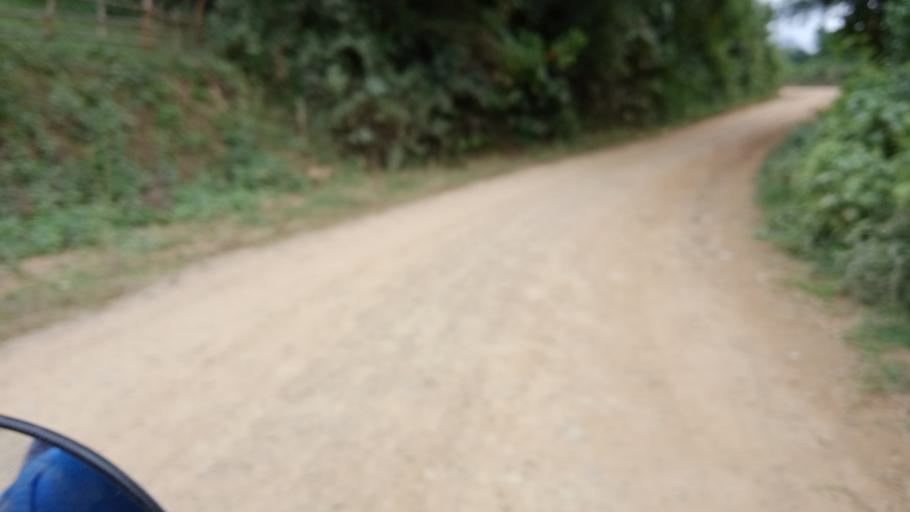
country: LA
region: Xiangkhoang
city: Phonsavan
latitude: 19.0935
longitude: 102.9970
